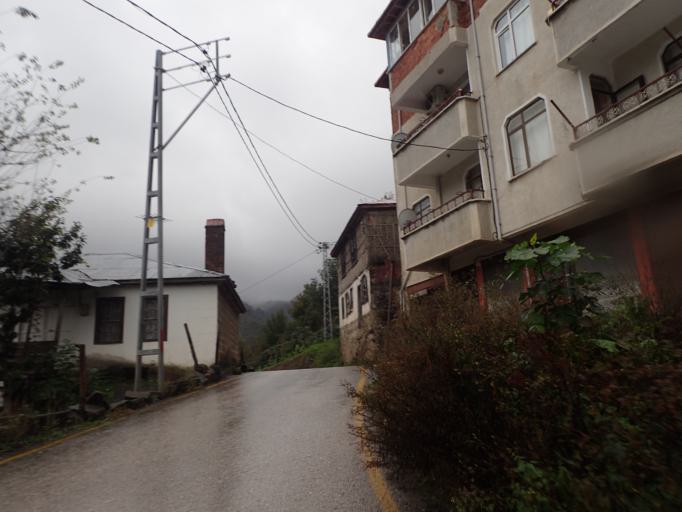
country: TR
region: Ordu
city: Persembe
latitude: 41.0409
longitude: 37.7299
